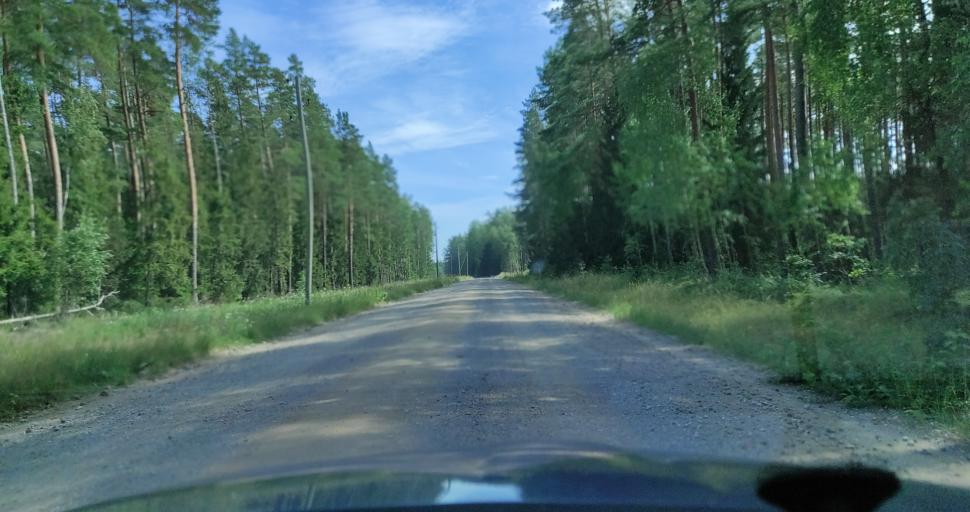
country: LV
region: Pavilostas
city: Pavilosta
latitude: 56.7645
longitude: 21.3155
